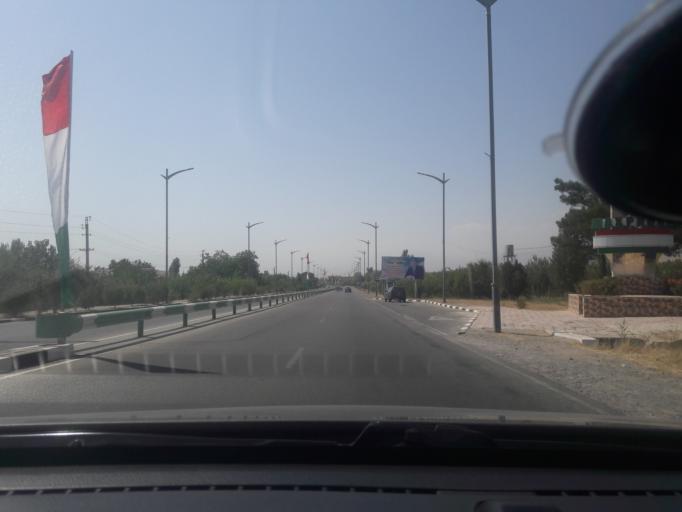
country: TJ
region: Republican Subordination
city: Hisor
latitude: 38.5605
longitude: 68.4503
